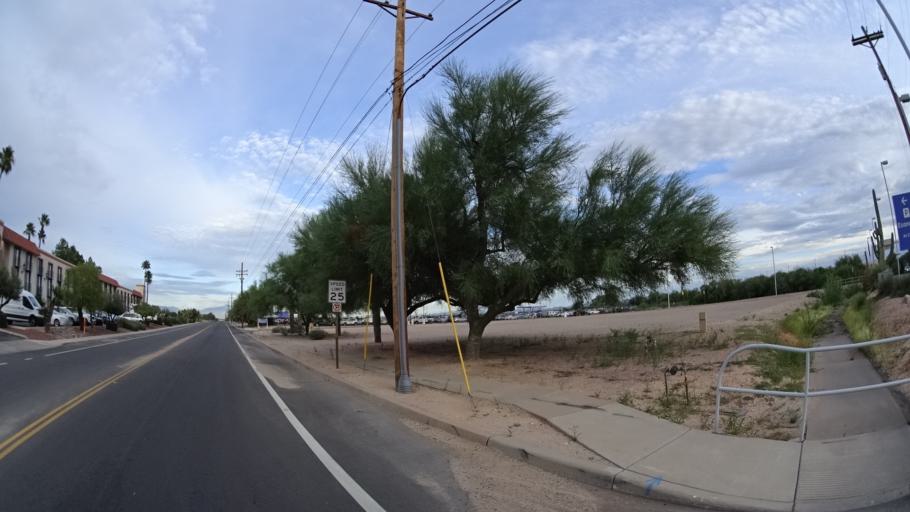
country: US
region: Arizona
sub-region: Pima County
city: Summit
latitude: 32.1231
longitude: -110.9344
